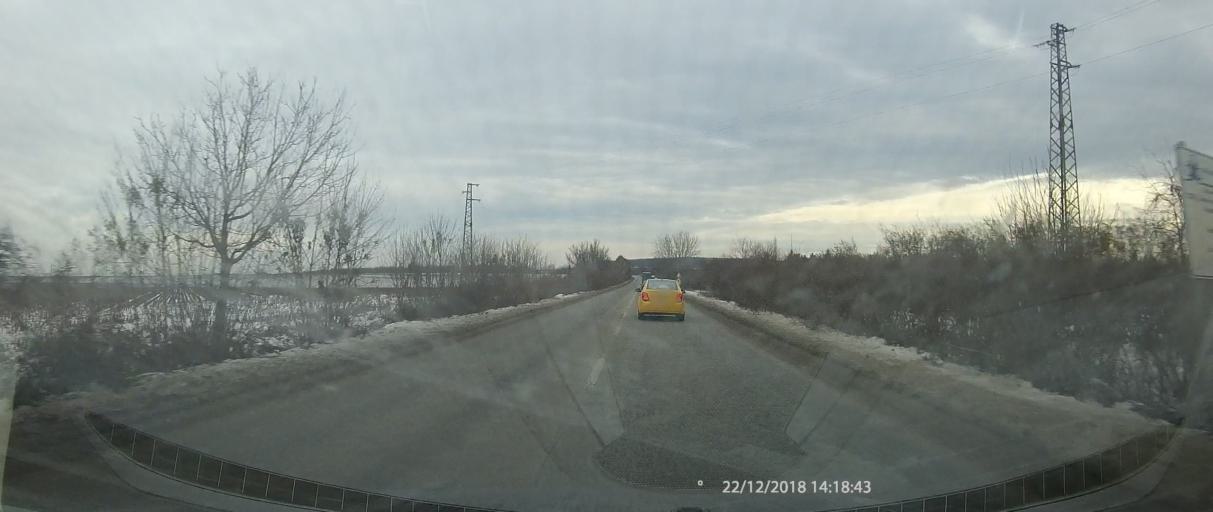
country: BG
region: Pleven
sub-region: Obshtina Pleven
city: Pleven
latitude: 43.4198
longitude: 24.7229
